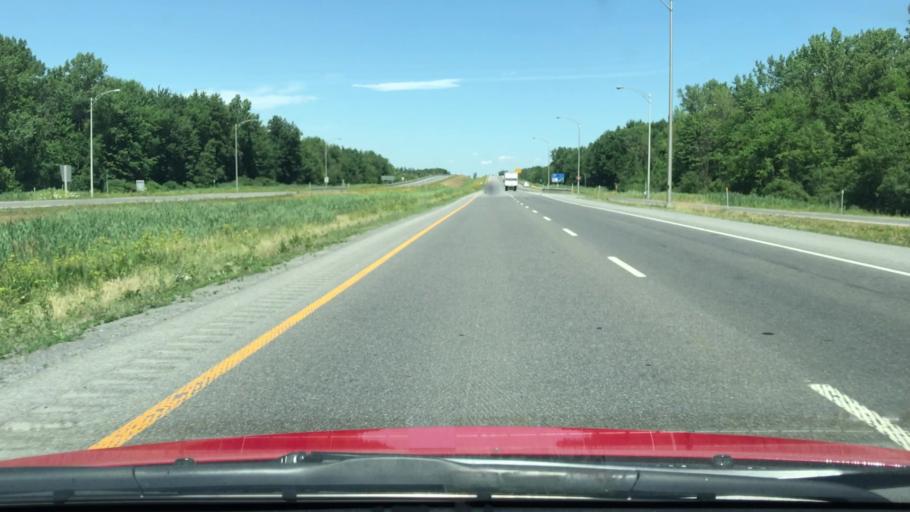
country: CA
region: Quebec
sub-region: Monteregie
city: Saint-Constant
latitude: 45.3798
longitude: -73.6143
